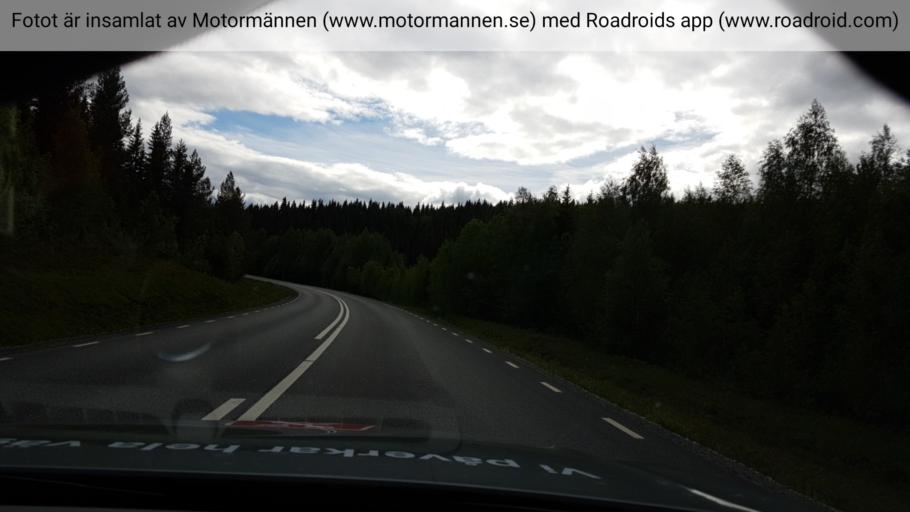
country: SE
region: Jaemtland
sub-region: Stroemsunds Kommun
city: Stroemsund
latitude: 64.1023
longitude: 15.5858
